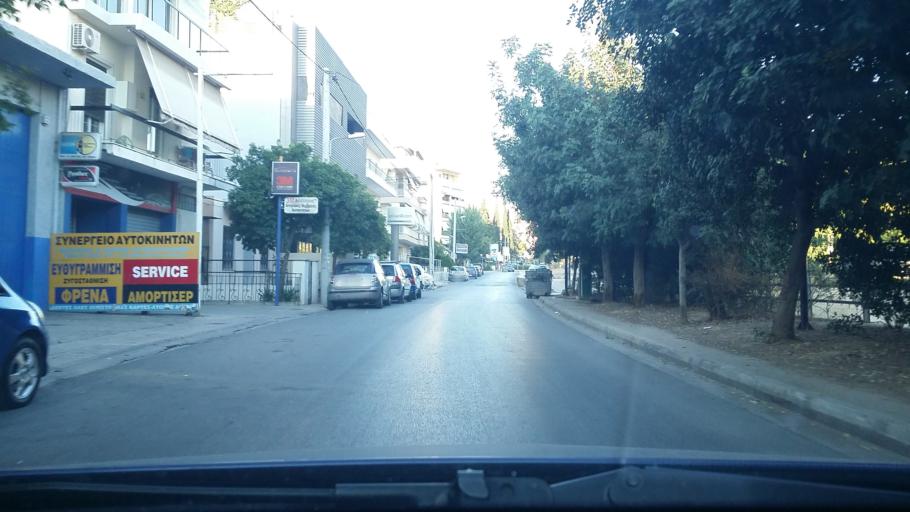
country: GR
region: Attica
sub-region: Nomarchia Athinas
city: Nea Chalkidona
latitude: 38.0252
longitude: 23.7297
